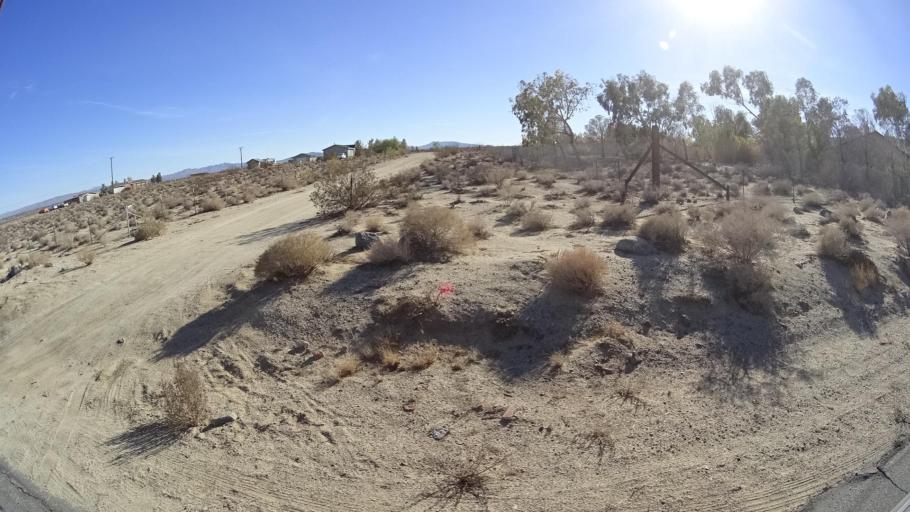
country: US
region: California
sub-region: Kern County
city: Inyokern
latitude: 35.6812
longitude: -117.8528
